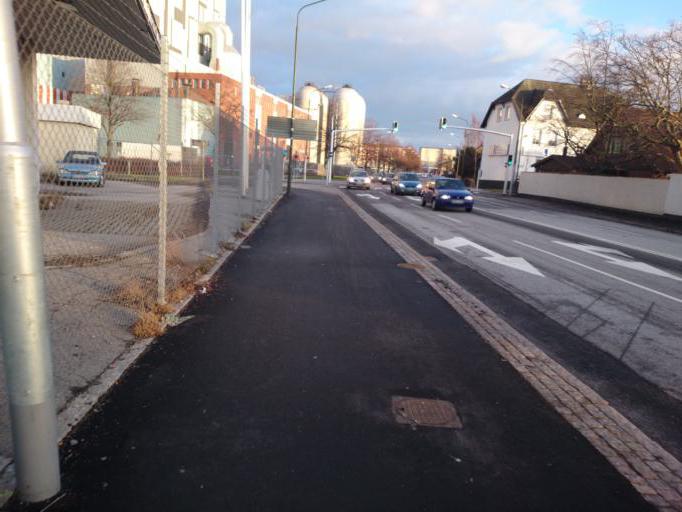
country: SE
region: Skane
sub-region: Malmo
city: Malmoe
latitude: 55.5781
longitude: 13.0094
